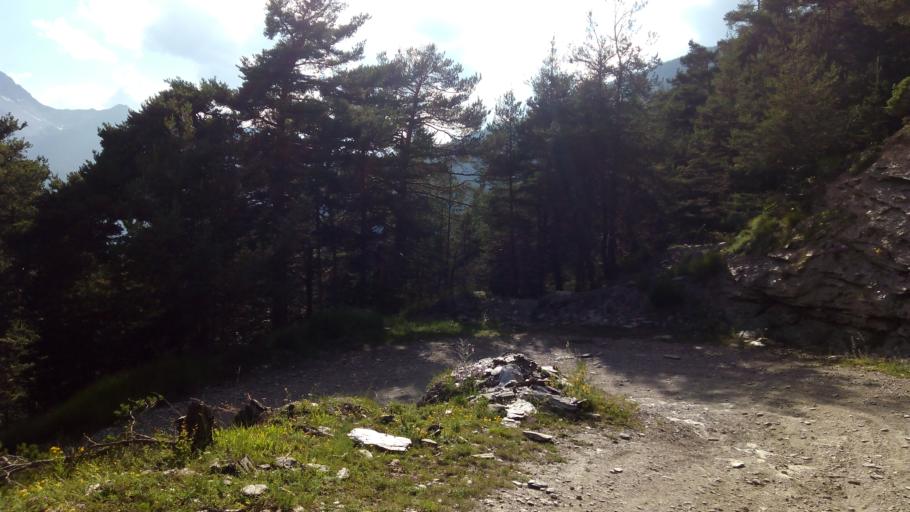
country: IT
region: Piedmont
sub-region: Provincia di Torino
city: Oulx
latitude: 45.0549
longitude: 6.7817
